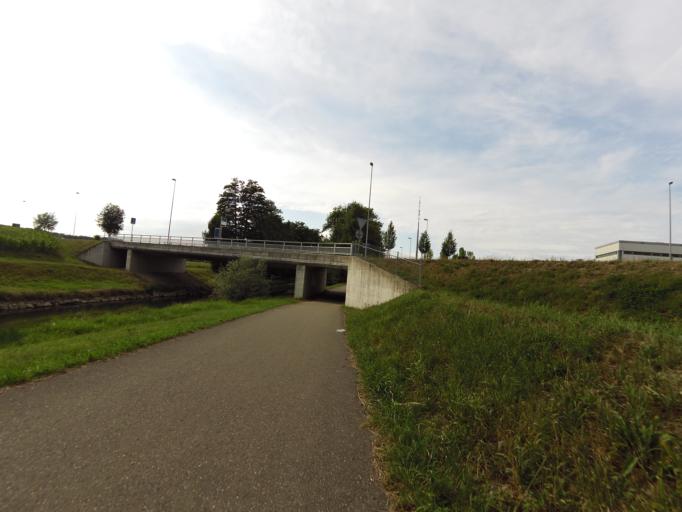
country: CH
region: Zurich
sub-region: Bezirk Buelach
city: Glattbrugg / Rohr/Platten-Balsberg
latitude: 47.4439
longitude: 8.5505
